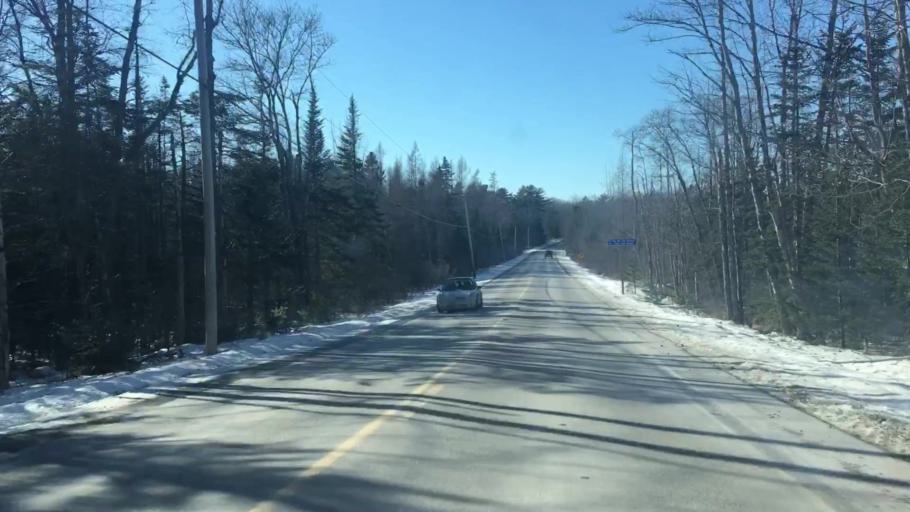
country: US
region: Maine
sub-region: Hancock County
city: Sedgwick
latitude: 44.3813
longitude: -68.6529
